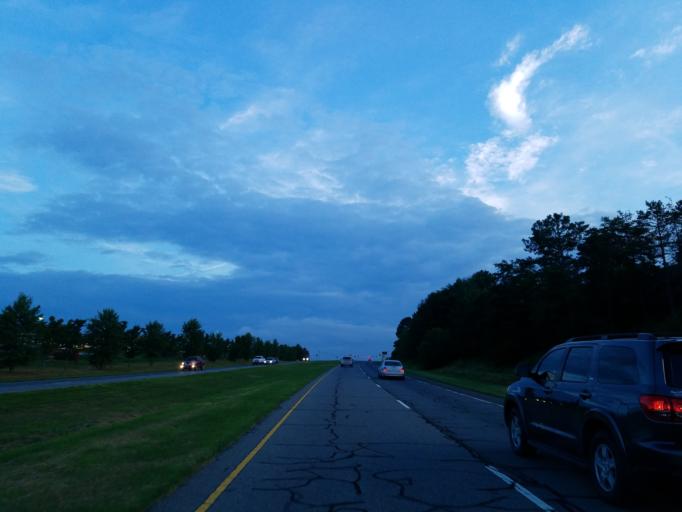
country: US
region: Georgia
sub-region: Gilmer County
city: Ellijay
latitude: 34.6606
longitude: -84.4903
